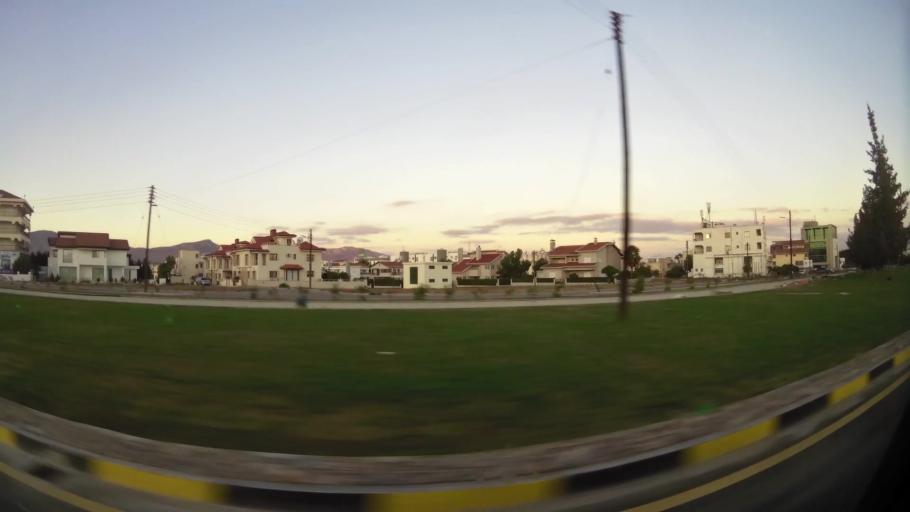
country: CY
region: Lefkosia
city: Nicosia
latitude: 35.2078
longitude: 33.3242
